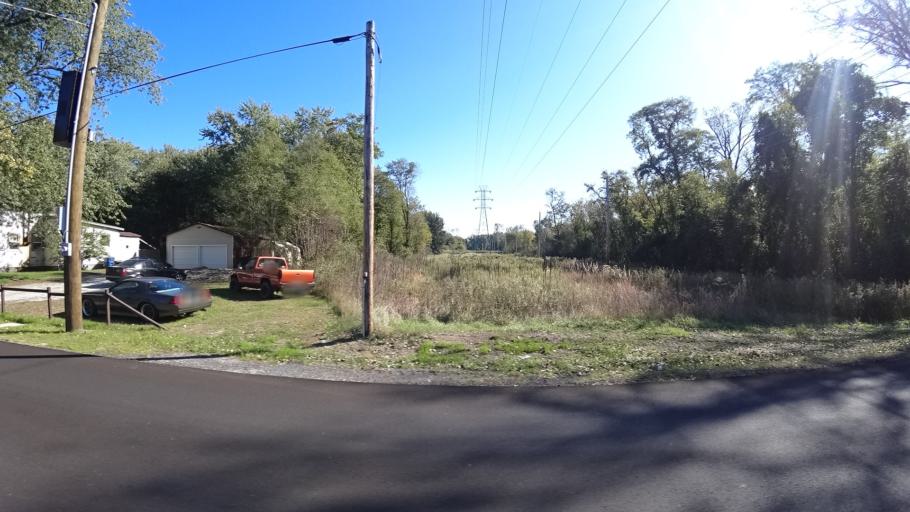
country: US
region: Indiana
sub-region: LaPorte County
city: Michigan City
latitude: 41.6981
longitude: -86.9140
